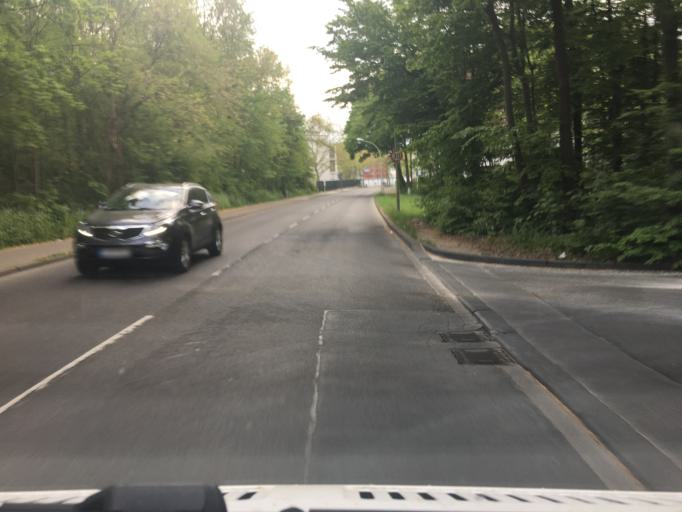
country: DE
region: North Rhine-Westphalia
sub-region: Regierungsbezirk Koln
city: Mengenich
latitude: 50.9643
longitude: 6.8786
